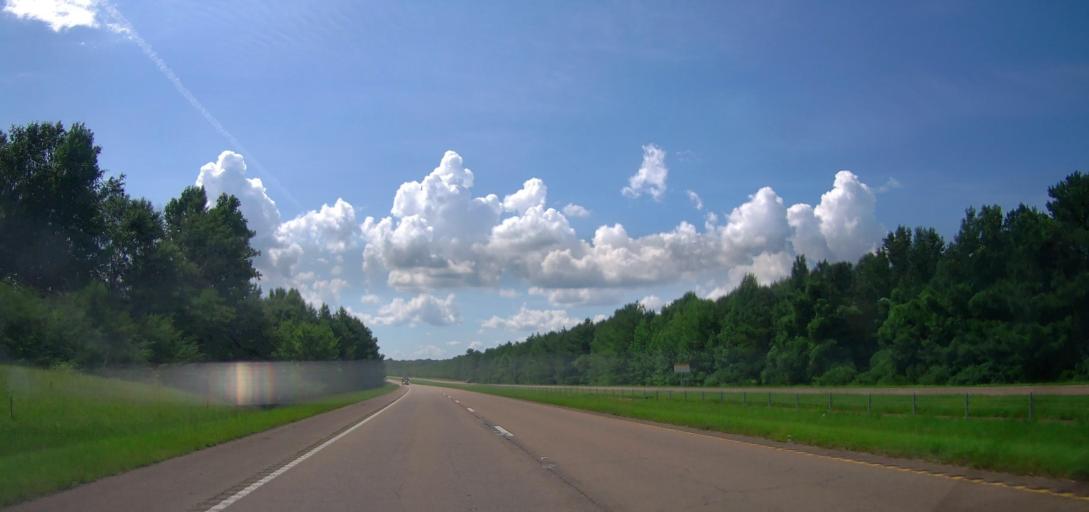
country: US
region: Mississippi
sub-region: Lowndes County
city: New Hope
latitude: 33.5039
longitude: -88.3115
